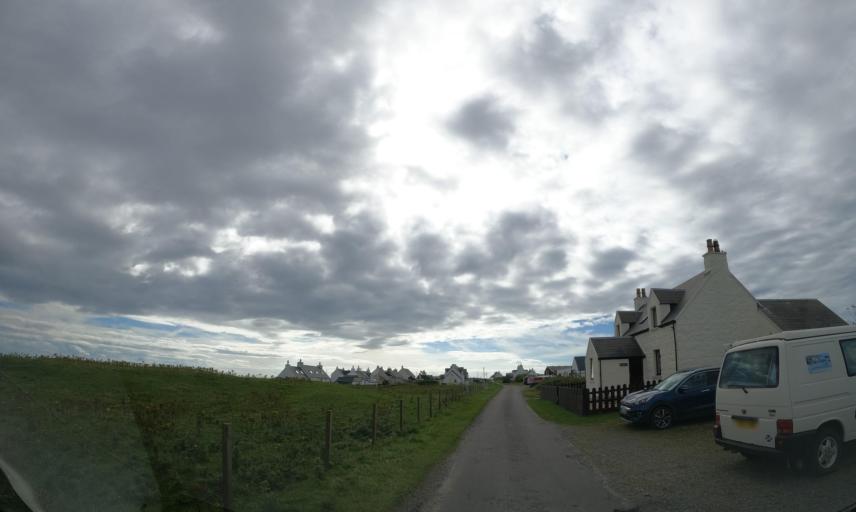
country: GB
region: Scotland
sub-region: Eilean Siar
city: Barra
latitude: 56.4685
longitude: -6.8971
